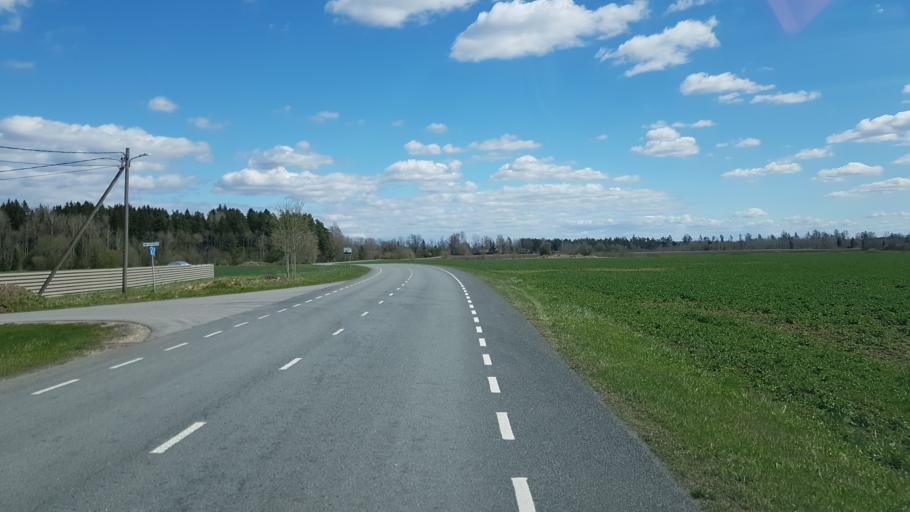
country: EE
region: Viljandimaa
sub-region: Viiratsi vald
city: Viiratsi
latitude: 58.3590
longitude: 25.6527
